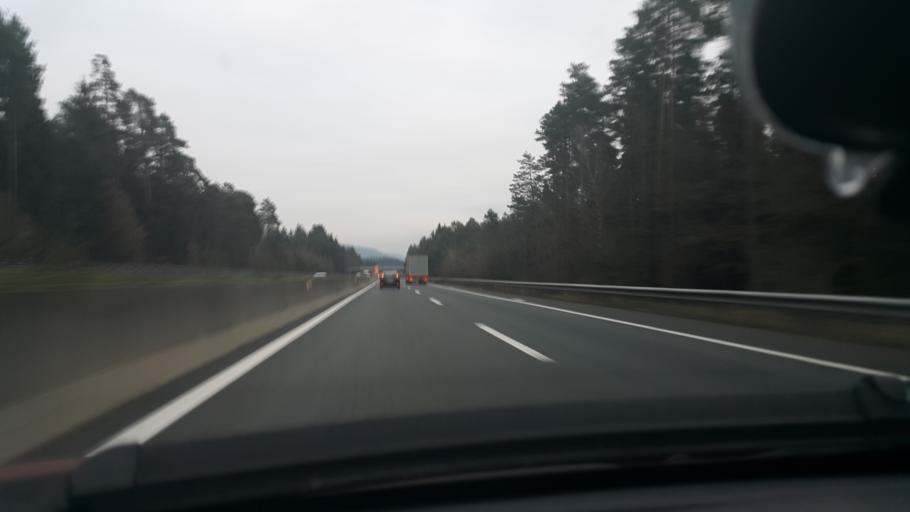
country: AT
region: Carinthia
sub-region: Politischer Bezirk Klagenfurt Land
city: Poggersdorf
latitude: 46.6417
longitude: 14.4779
